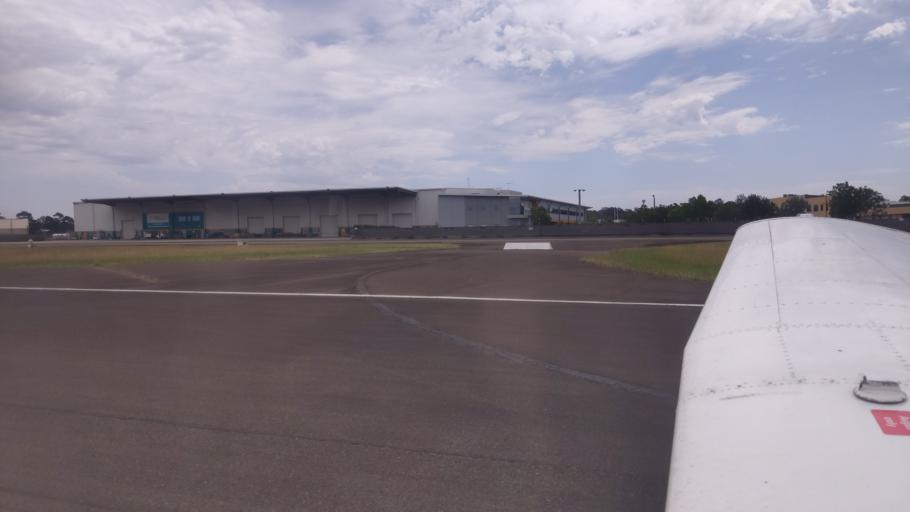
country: AU
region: New South Wales
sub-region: Bankstown
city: Milperra
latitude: -33.9245
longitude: 150.9945
